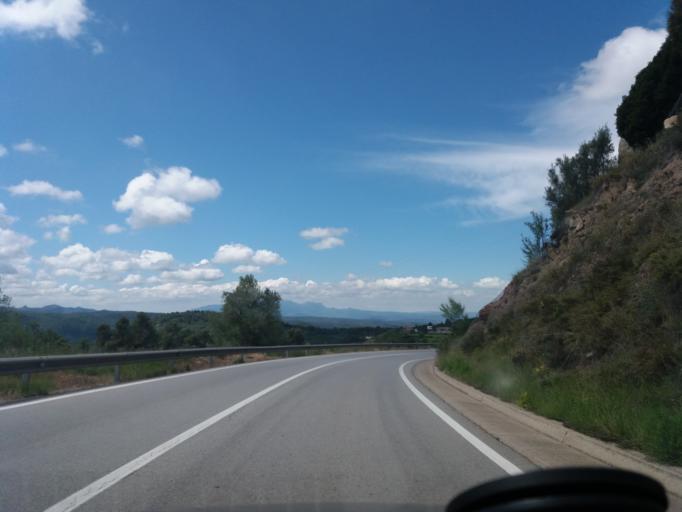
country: ES
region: Catalonia
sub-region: Provincia de Barcelona
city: Artes
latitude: 41.7885
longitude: 1.9947
